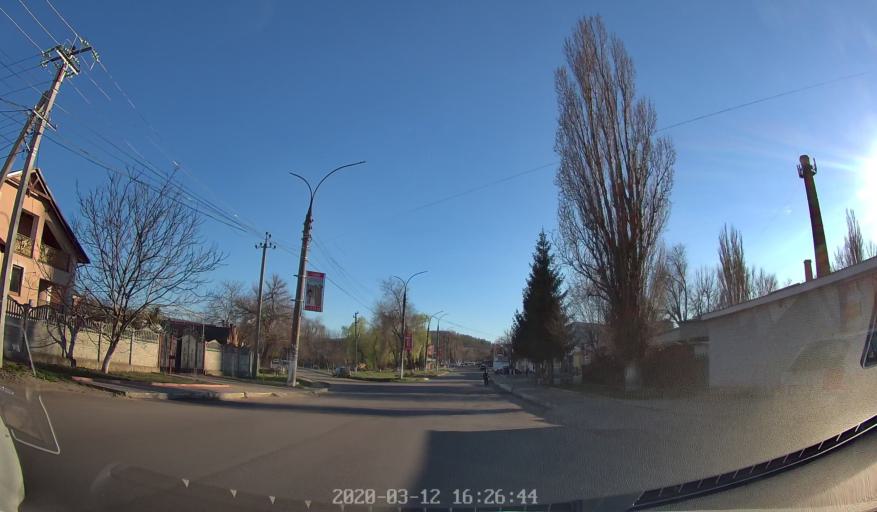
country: MD
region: Anenii Noi
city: Anenii Noi
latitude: 46.8799
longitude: 29.2323
